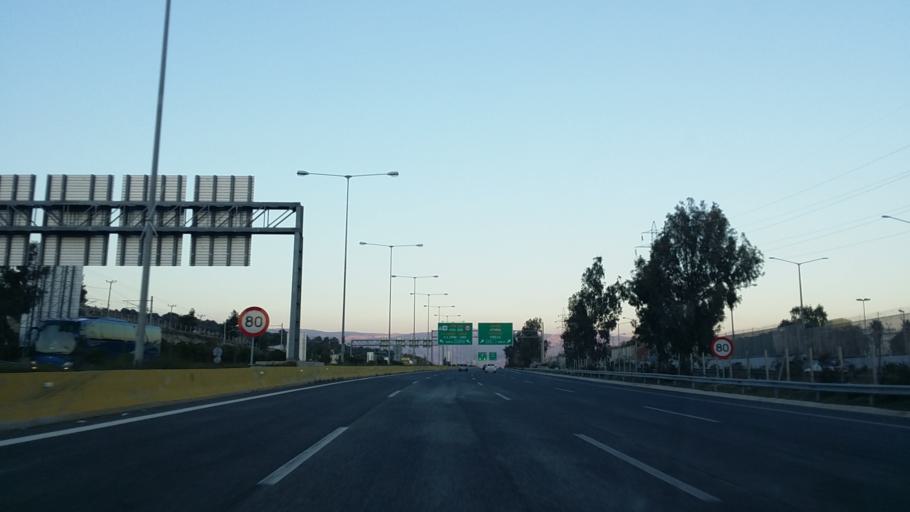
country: GR
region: Attica
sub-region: Nomarchia Dytikis Attikis
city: Mandra
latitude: 38.0462
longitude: 23.4994
